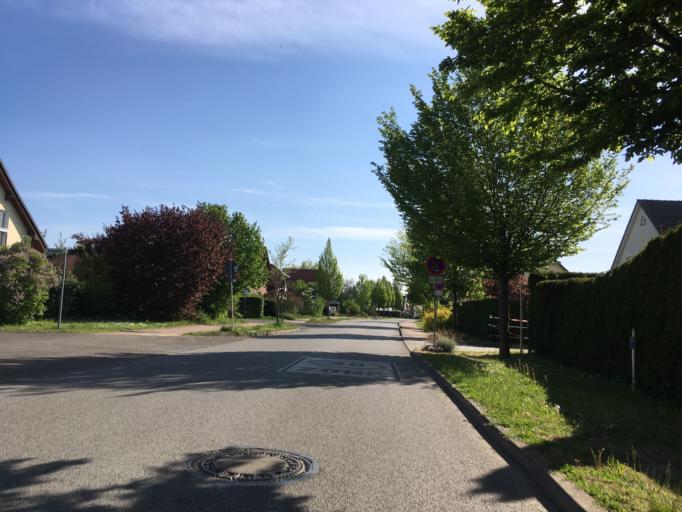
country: DE
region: Berlin
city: Buch
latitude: 52.6578
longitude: 13.5194
